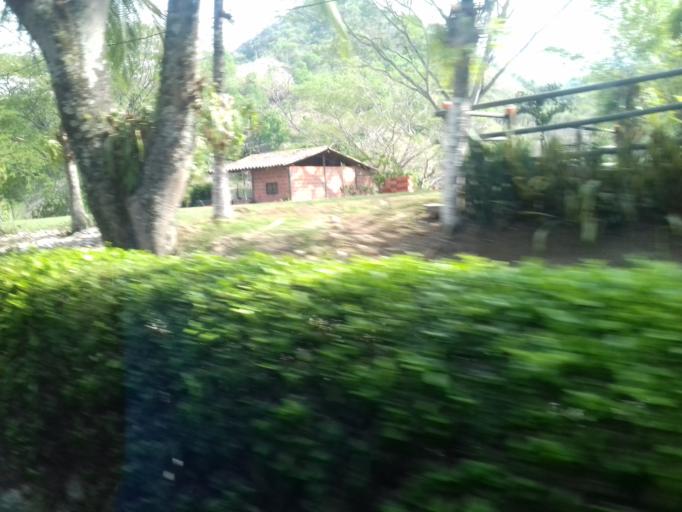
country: CO
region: Antioquia
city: Venecia
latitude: 5.9704
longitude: -75.8290
